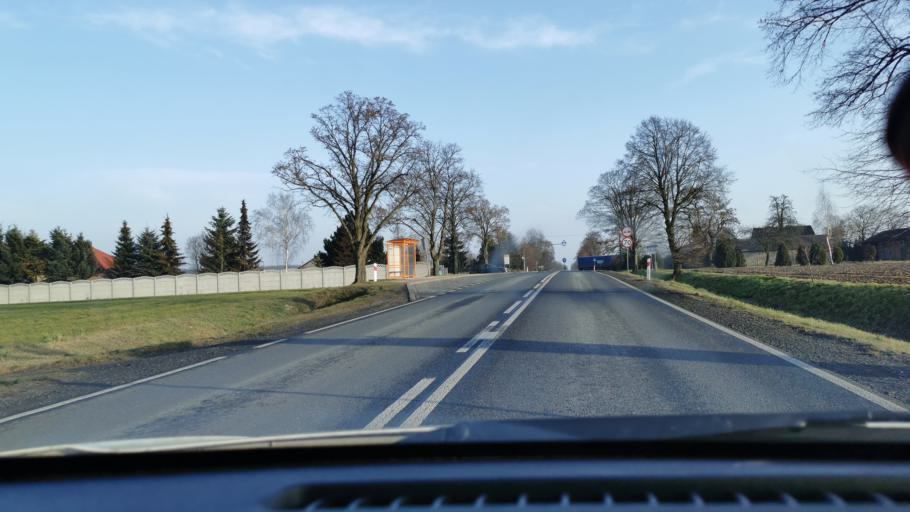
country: PL
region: Lodz Voivodeship
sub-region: Powiat sieradzki
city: Blaszki
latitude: 51.6409
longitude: 18.4994
